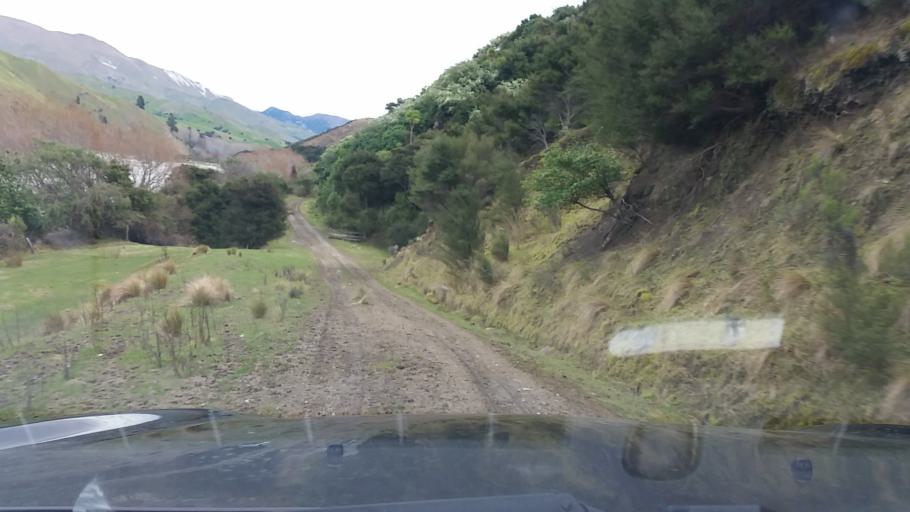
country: NZ
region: Marlborough
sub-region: Marlborough District
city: Blenheim
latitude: -41.8838
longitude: 174.0819
